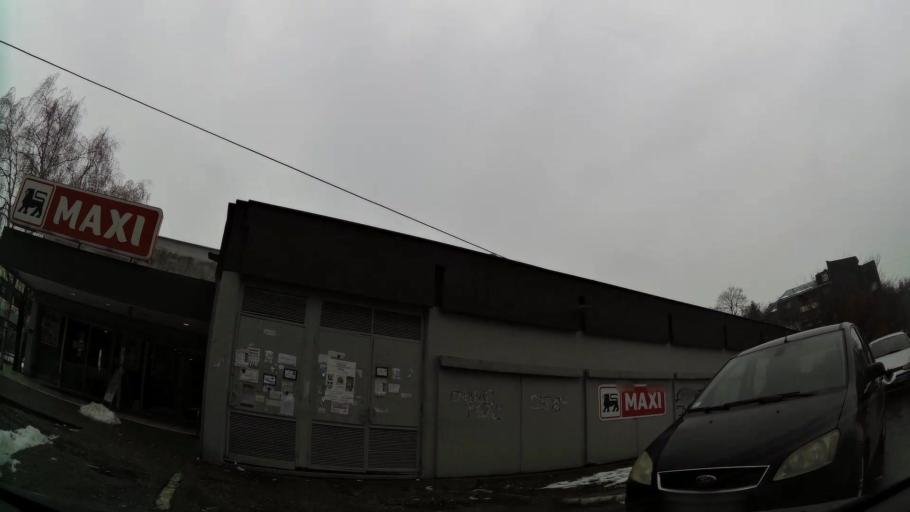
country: RS
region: Central Serbia
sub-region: Belgrade
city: Vozdovac
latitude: 44.7498
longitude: 20.4988
